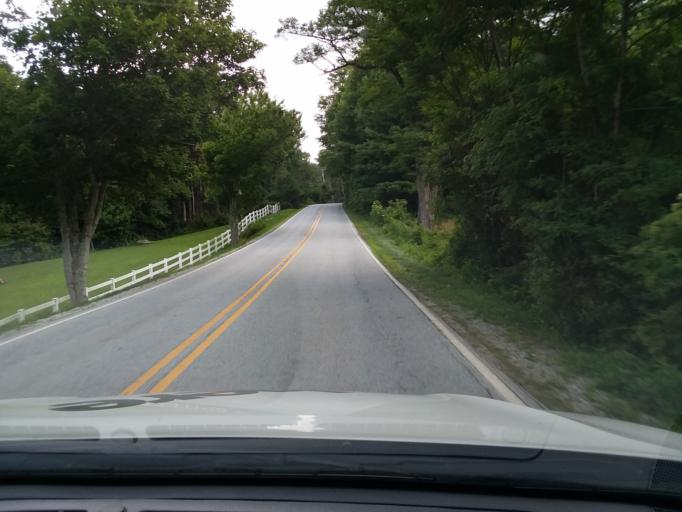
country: US
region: Georgia
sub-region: Rabun County
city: Mountain City
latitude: 35.0379
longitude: -83.2535
